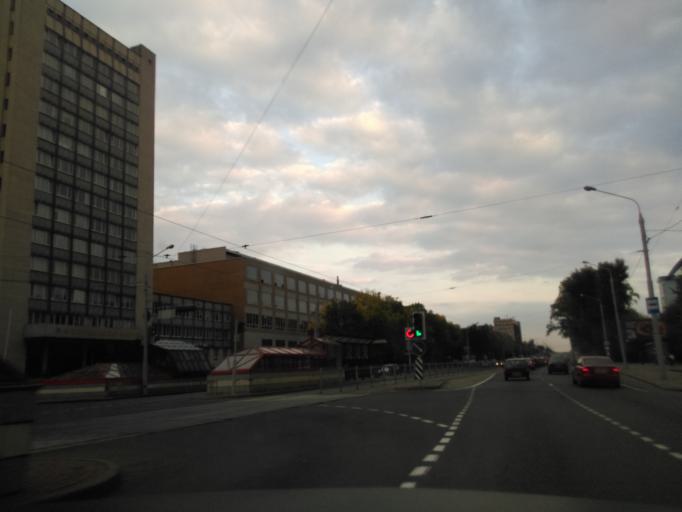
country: BY
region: Minsk
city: Minsk
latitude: 53.8981
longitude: 27.6052
